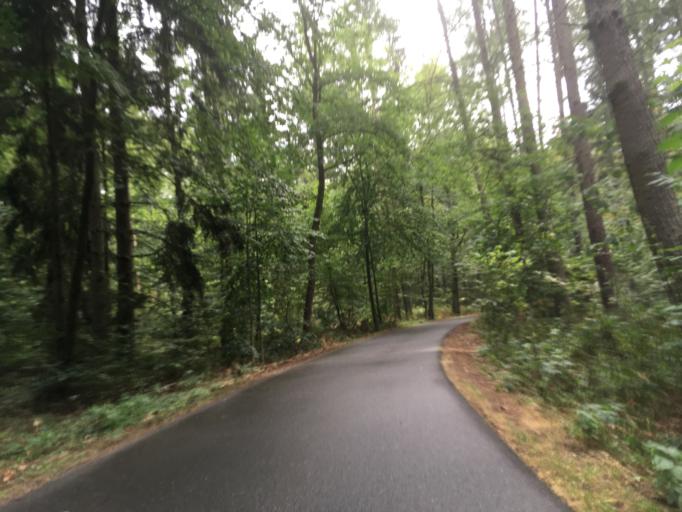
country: DE
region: Brandenburg
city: Chorin
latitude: 52.9225
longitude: 13.8572
